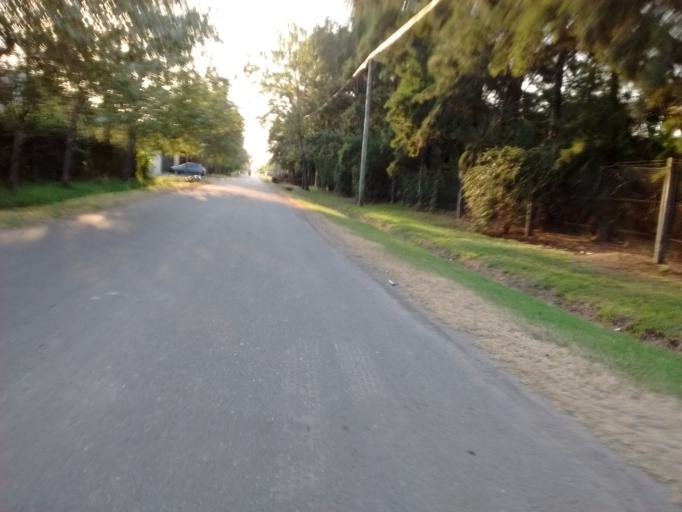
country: AR
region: Santa Fe
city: Funes
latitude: -32.9161
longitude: -60.7579
